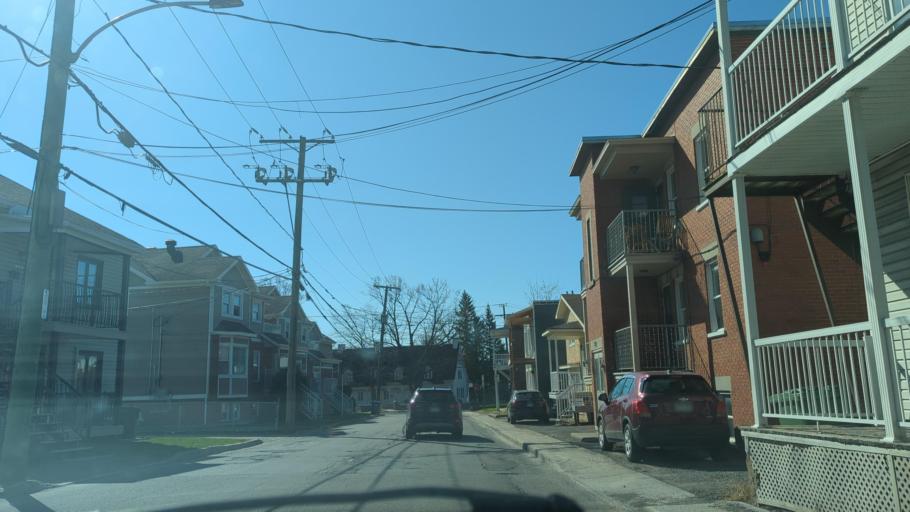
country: CA
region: Quebec
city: Quebec
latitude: 46.8516
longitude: -71.2113
